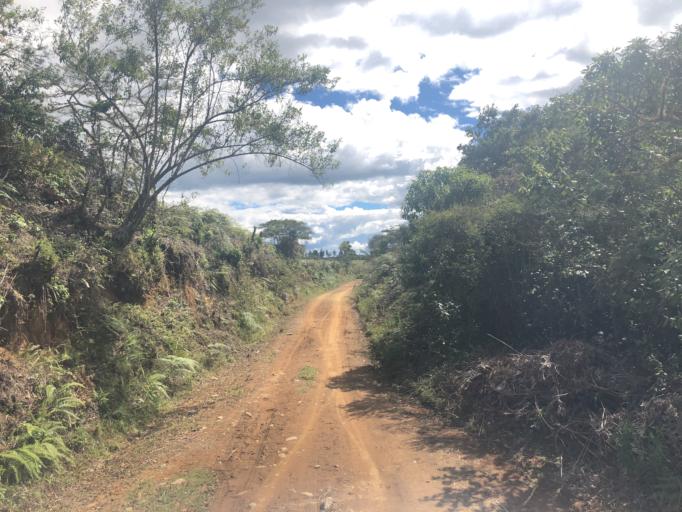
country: CO
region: Cauca
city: Silvia
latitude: 2.6837
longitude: -76.4373
